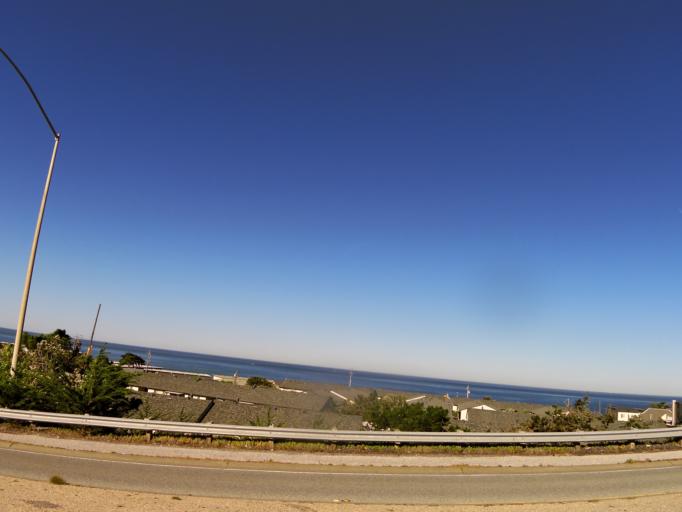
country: US
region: California
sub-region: San Mateo County
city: Broadmoor
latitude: 37.6533
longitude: -122.4904
